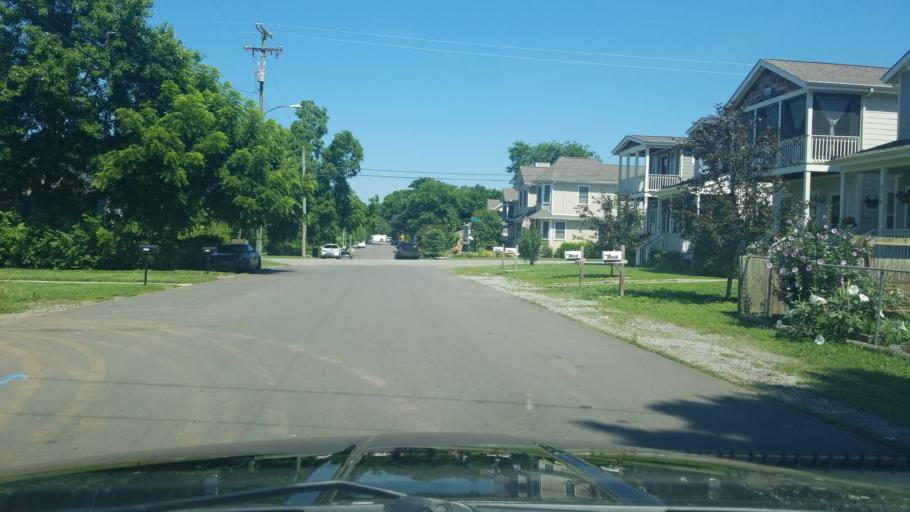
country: US
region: Tennessee
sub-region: Davidson County
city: Belle Meade
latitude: 36.1647
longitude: -86.8608
